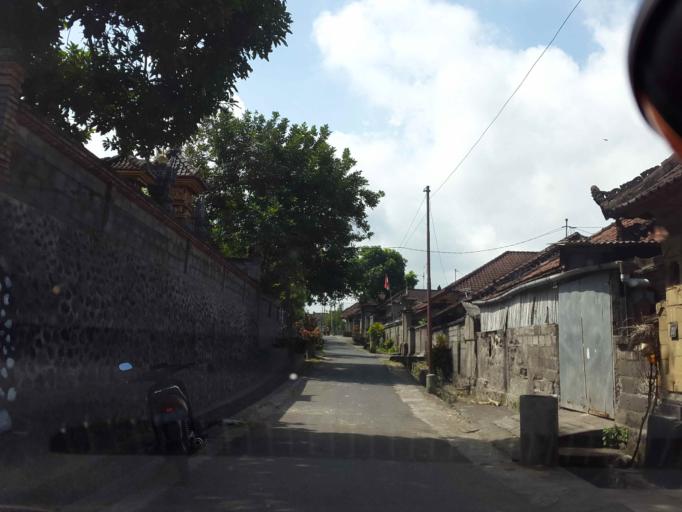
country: ID
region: Bali
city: Klungkung
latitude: -8.5509
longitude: 115.3662
